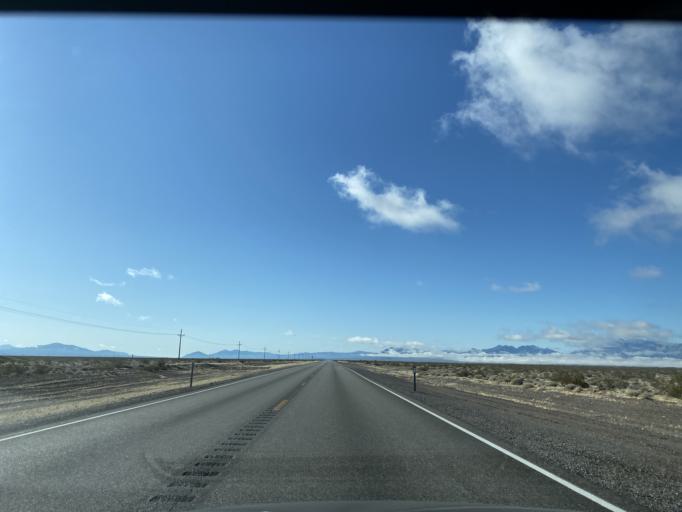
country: US
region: Nevada
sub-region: Nye County
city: Beatty
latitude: 36.6134
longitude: -116.4057
